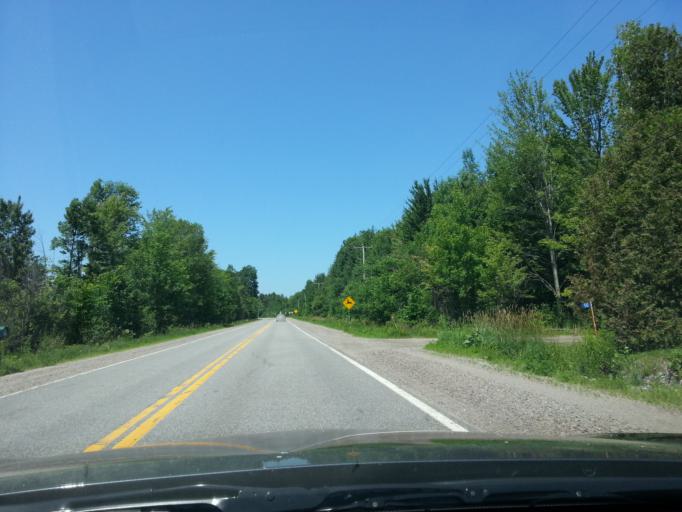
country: CA
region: Ontario
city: Arnprior
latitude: 45.5482
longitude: -76.3519
